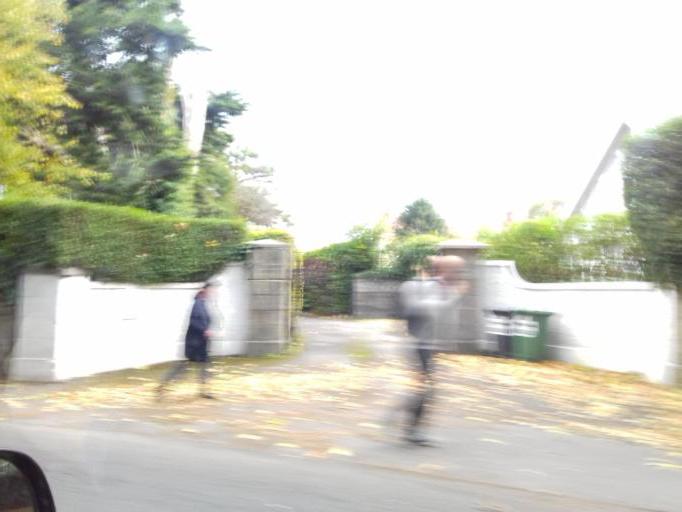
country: IE
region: Leinster
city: Loughlinstown
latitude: 53.2402
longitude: -6.1224
